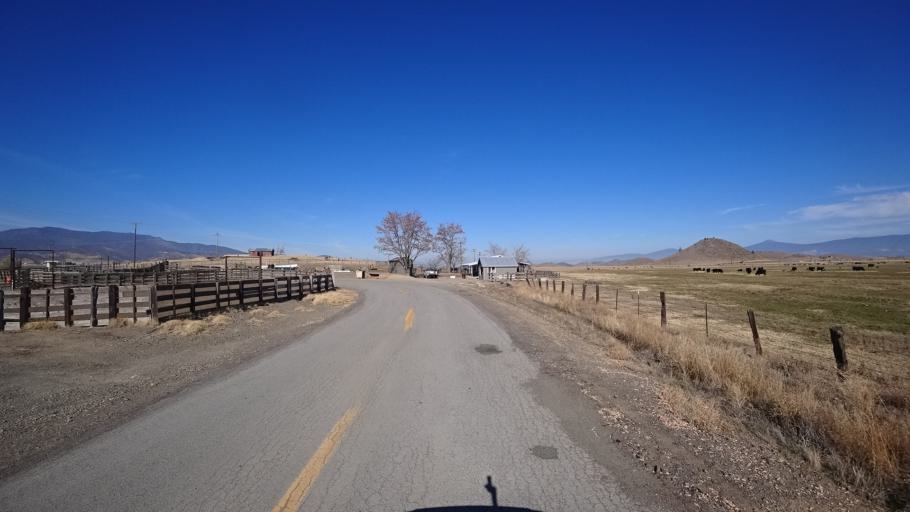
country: US
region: California
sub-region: Siskiyou County
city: Weed
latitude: 41.5265
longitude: -122.5308
